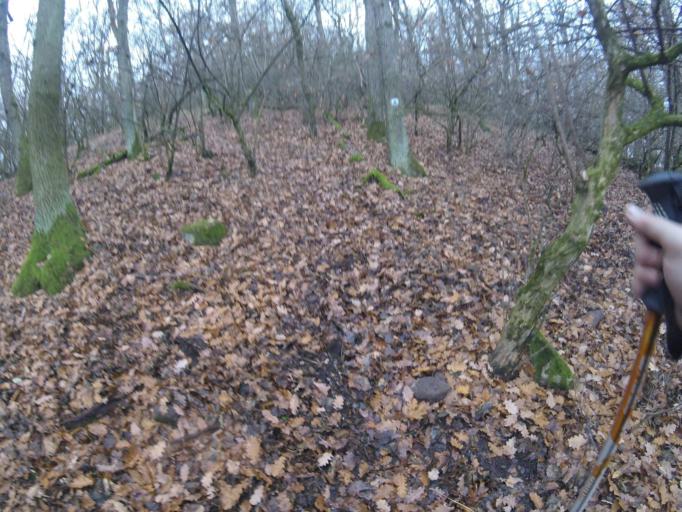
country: HU
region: Pest
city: Szob
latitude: 47.8750
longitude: 18.8292
